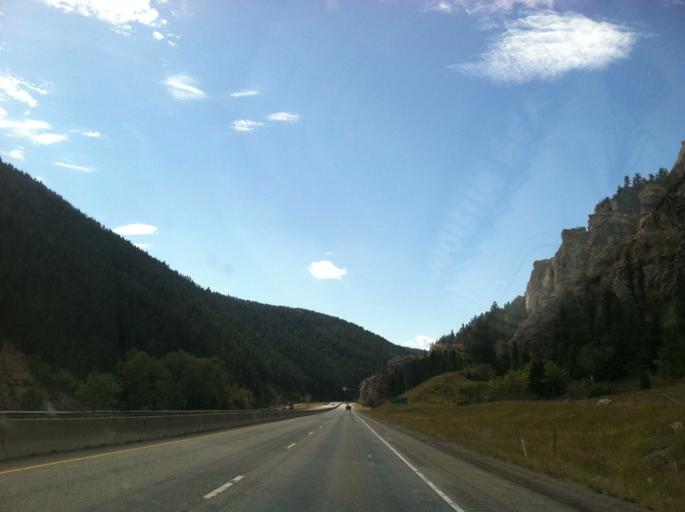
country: US
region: Montana
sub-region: Gallatin County
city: Bozeman
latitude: 45.6420
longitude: -110.9049
